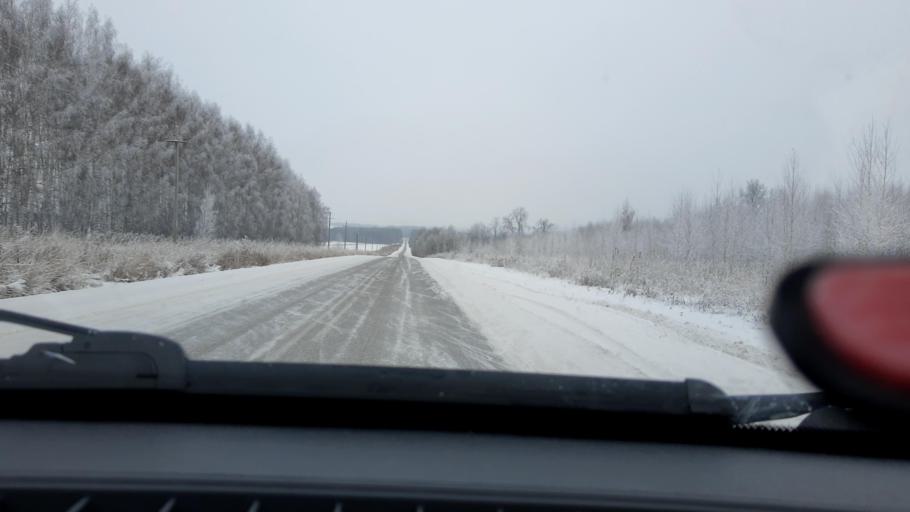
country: RU
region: Bashkortostan
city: Iglino
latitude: 54.6599
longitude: 56.4241
